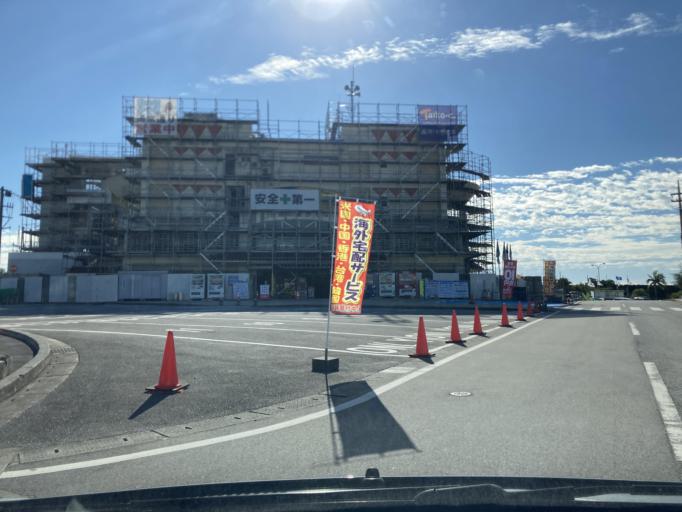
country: JP
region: Okinawa
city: Okinawa
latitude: 26.3685
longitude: 127.7738
